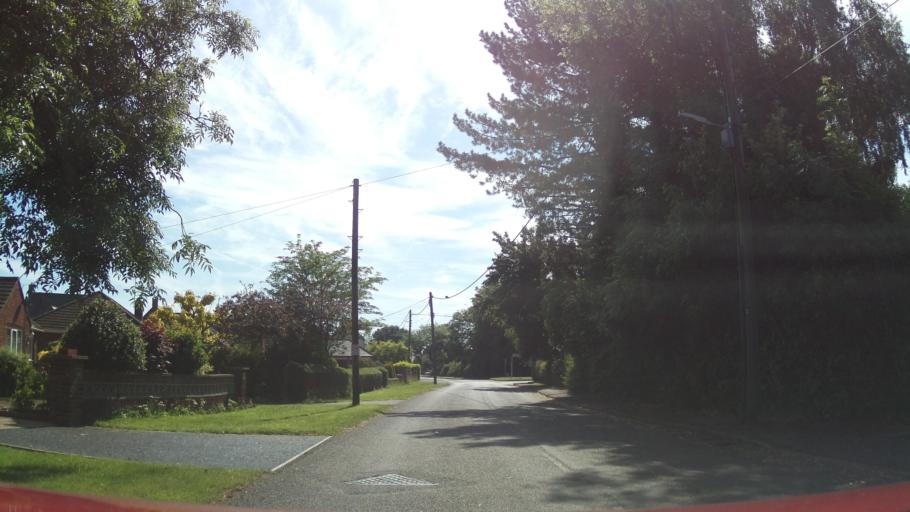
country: GB
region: England
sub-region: Lincolnshire
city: Skellingthorpe
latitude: 53.1316
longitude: -0.6371
